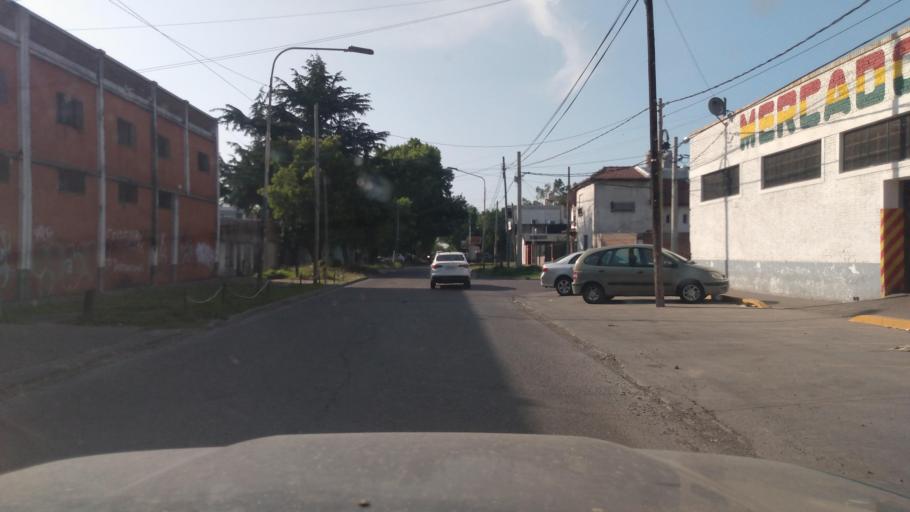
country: AR
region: Buenos Aires
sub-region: Partido de Moron
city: Moron
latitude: -34.6556
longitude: -58.5987
